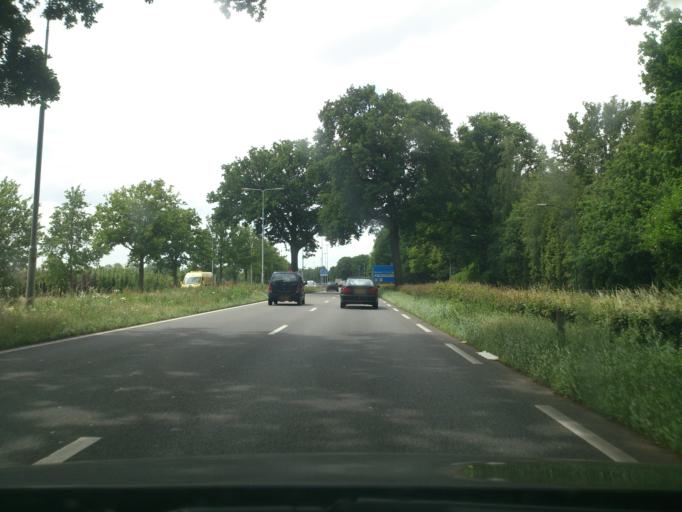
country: NL
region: North Brabant
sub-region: Gemeente Oisterwijk
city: Oisterwijk
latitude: 51.5819
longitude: 5.1529
